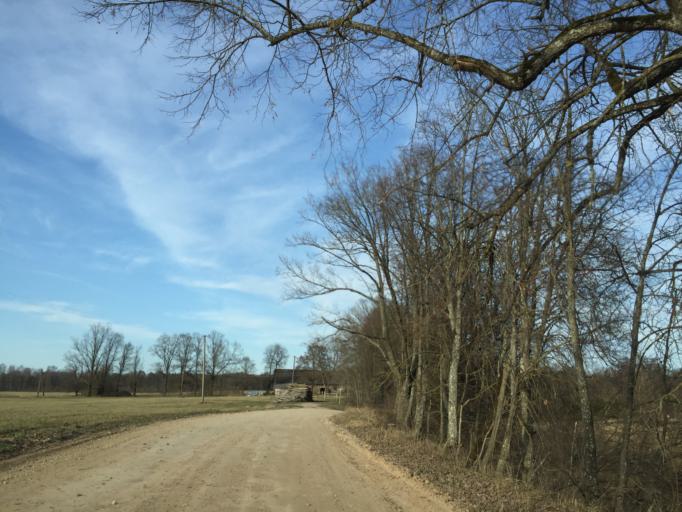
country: LV
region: Kegums
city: Kegums
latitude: 56.7977
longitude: 24.7325
